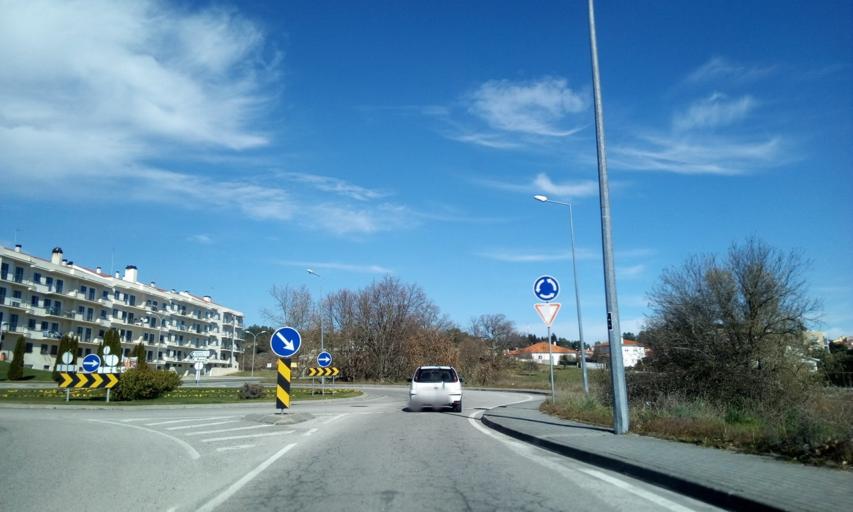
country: PT
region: Guarda
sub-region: Guarda
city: Sequeira
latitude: 40.5589
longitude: -7.2347
